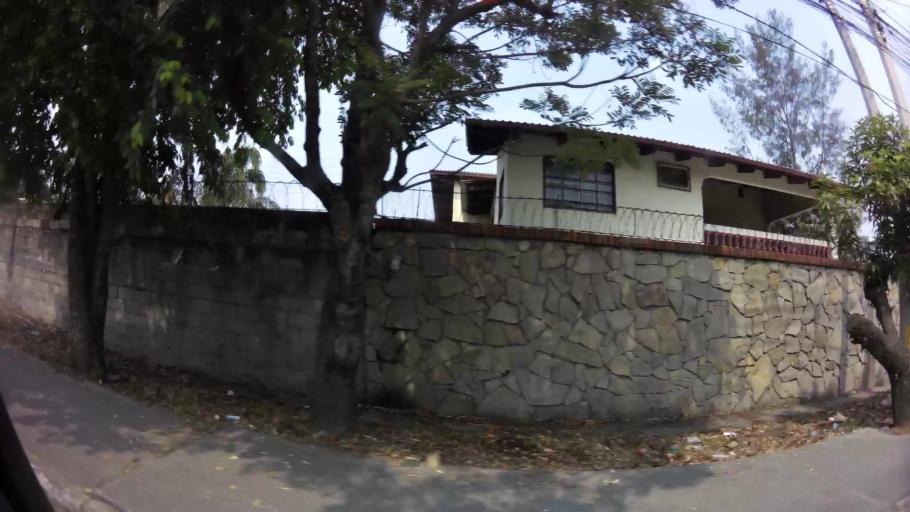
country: HN
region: Cortes
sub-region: San Pedro Sula
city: Pena Blanca
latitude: 15.5493
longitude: -88.0104
